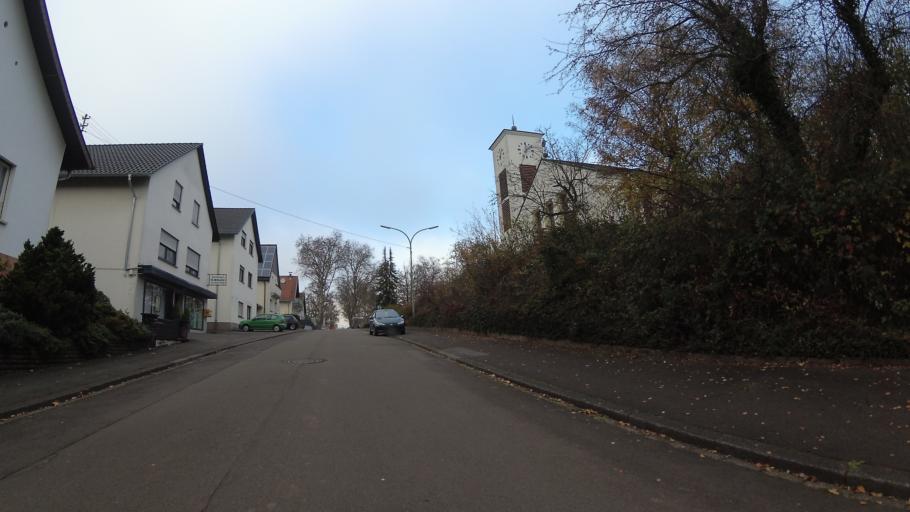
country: DE
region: Saarland
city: Schwalbach
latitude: 49.2982
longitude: 6.8034
